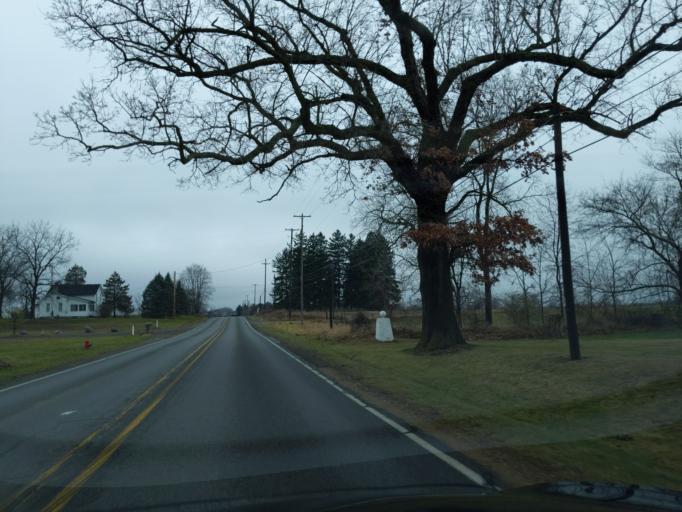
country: US
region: Michigan
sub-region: Jackson County
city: Jackson
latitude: 42.2766
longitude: -84.4655
